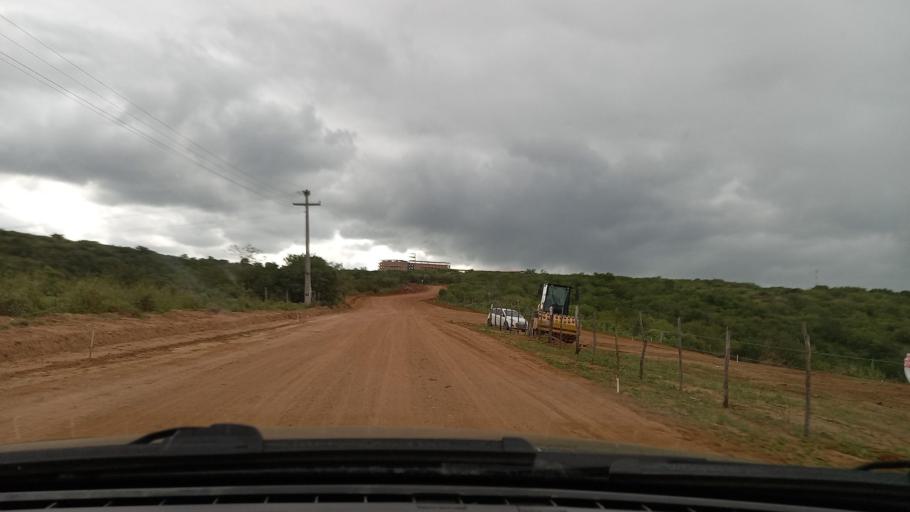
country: BR
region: Sergipe
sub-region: Caninde De Sao Francisco
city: Caninde de Sao Francisco
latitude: -9.6204
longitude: -37.7582
